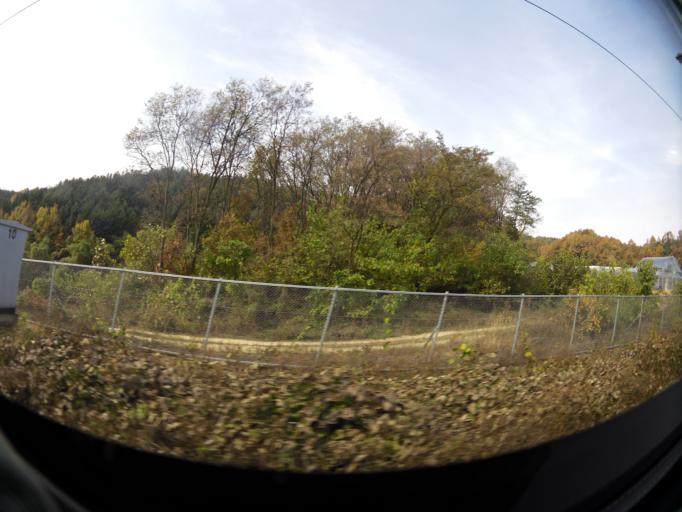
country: KR
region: Gyeongsangbuk-do
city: Gimcheon
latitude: 36.1792
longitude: 128.0074
